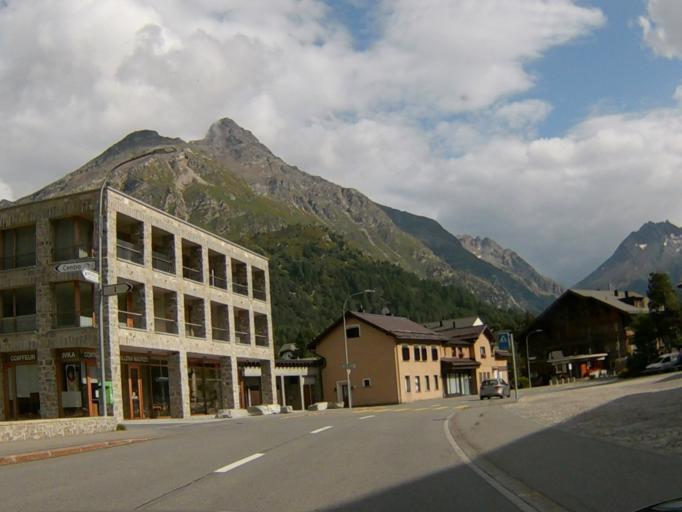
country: CH
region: Grisons
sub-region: Maloja District
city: Silvaplana
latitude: 46.4038
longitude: 9.6951
